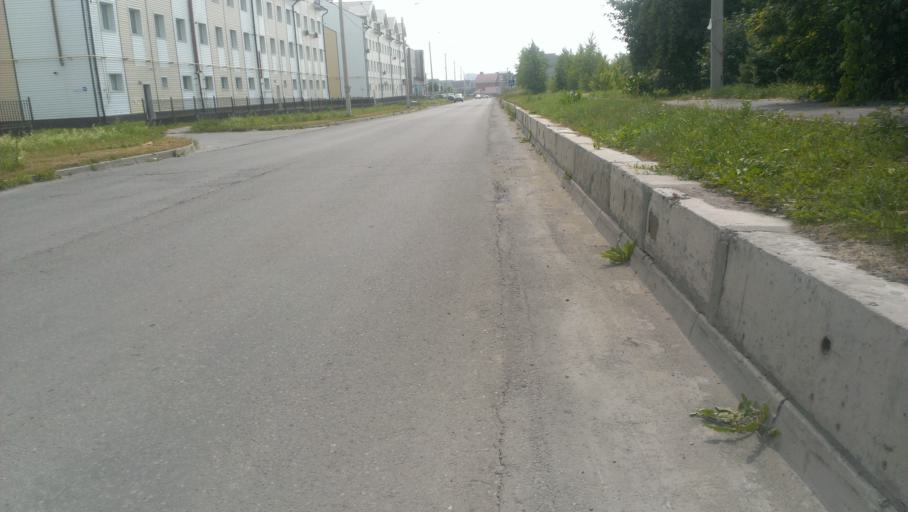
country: RU
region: Altai Krai
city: Novosilikatnyy
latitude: 53.3601
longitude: 83.6558
